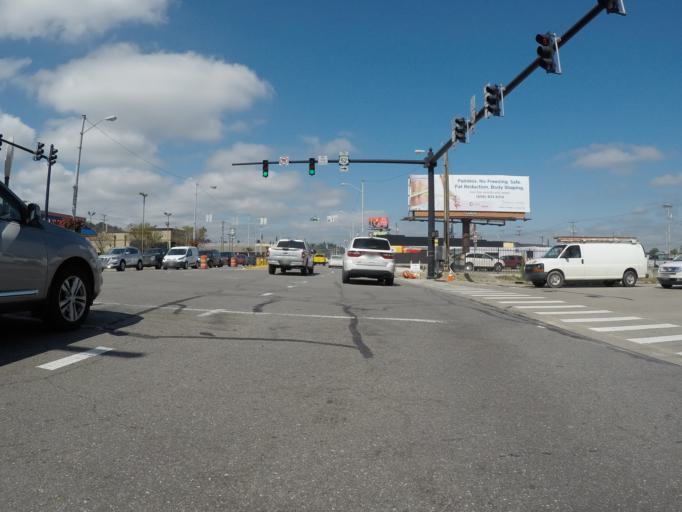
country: US
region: Kentucky
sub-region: Boyd County
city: Ashland
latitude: 38.4804
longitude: -82.6429
